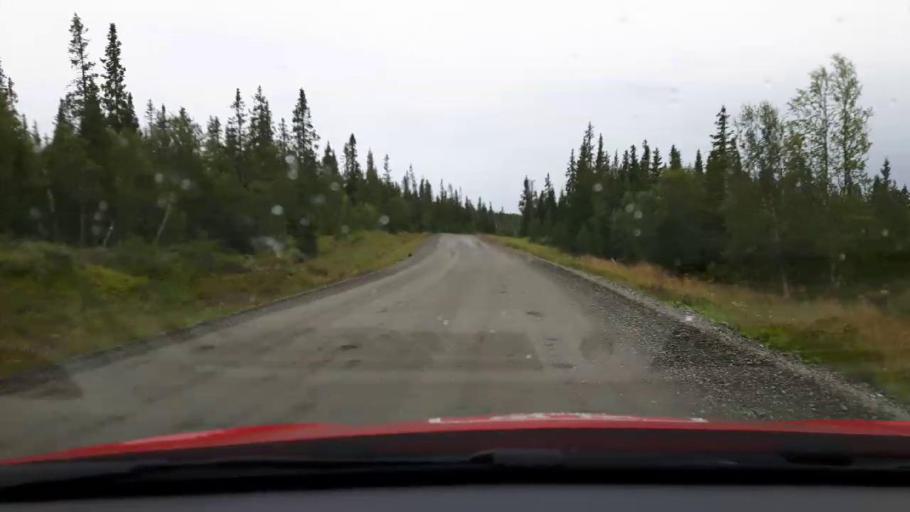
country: NO
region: Nord-Trondelag
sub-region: Meraker
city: Meraker
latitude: 63.5601
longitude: 12.3671
